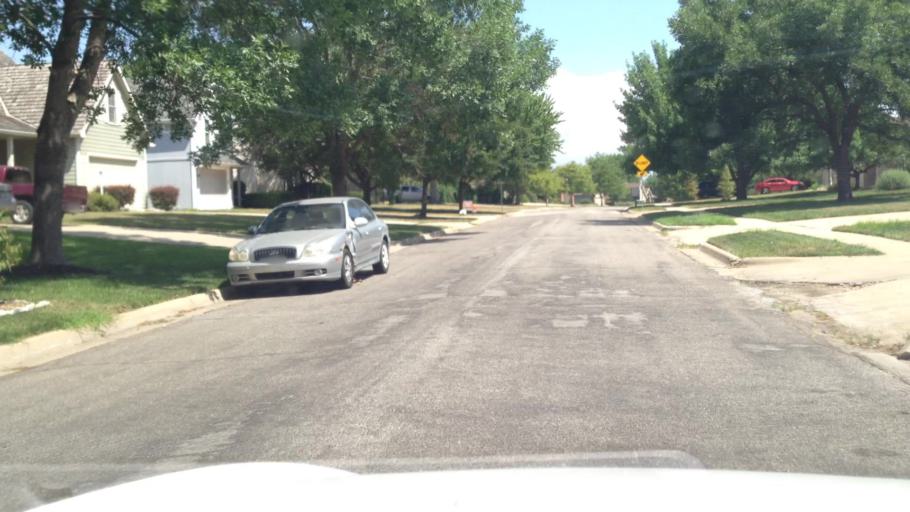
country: US
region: Kansas
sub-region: Douglas County
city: Lawrence
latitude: 38.9507
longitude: -95.3057
